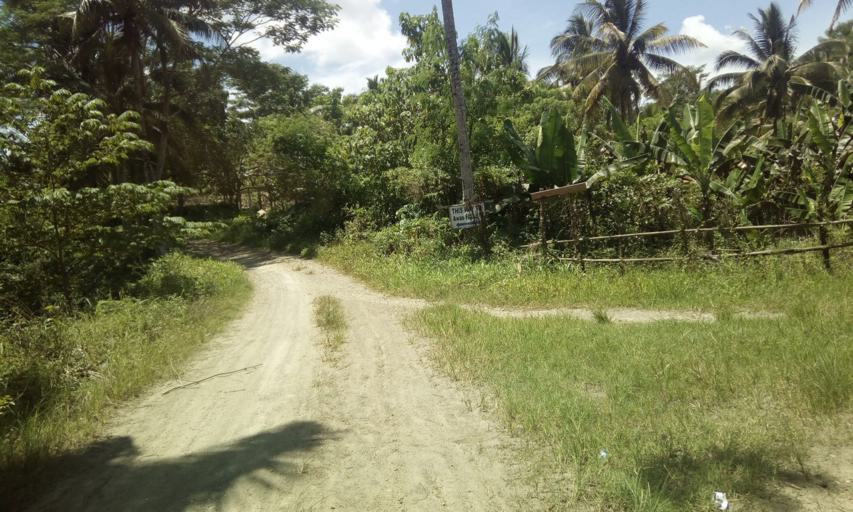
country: PH
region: Caraga
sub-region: Province of Agusan del Sur
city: Santa Josefa
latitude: 7.9538
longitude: 125.9886
